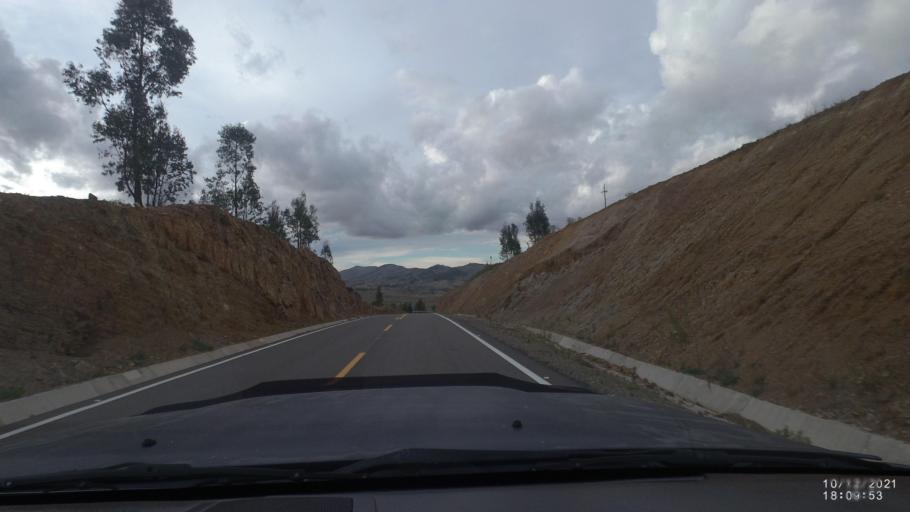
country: BO
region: Cochabamba
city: Tarata
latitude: -17.7920
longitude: -65.9549
